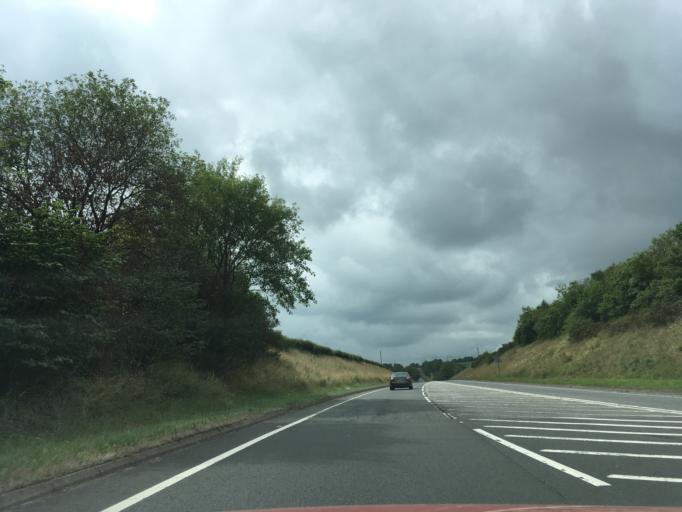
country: GB
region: Wales
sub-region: Carmarthenshire
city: Whitland
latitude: 51.8236
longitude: -4.5788
